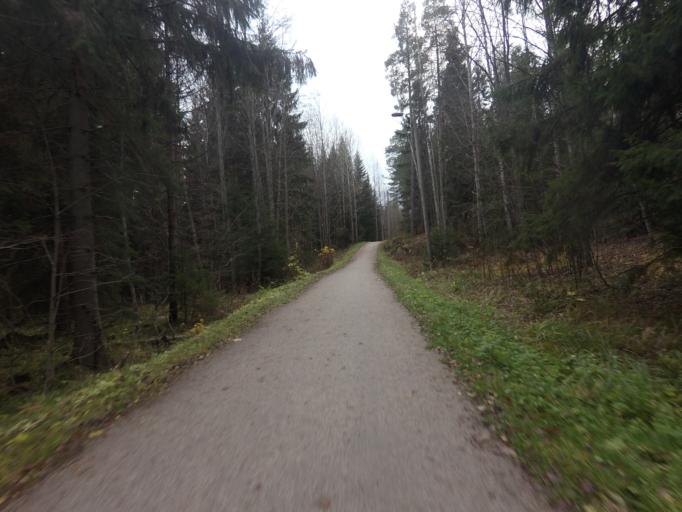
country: FI
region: Uusimaa
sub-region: Helsinki
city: Kauniainen
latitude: 60.1924
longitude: 24.6978
